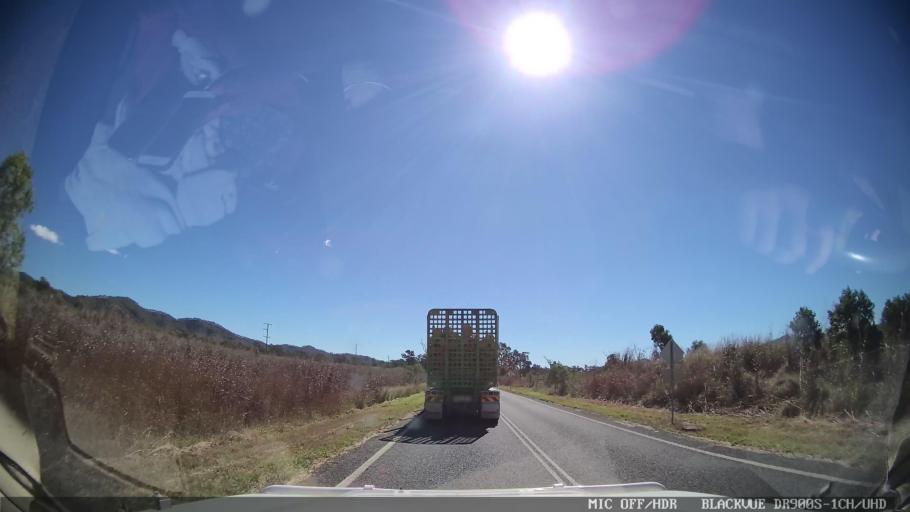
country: AU
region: Queensland
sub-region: Gladstone
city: Toolooa
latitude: -24.2717
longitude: 151.2752
